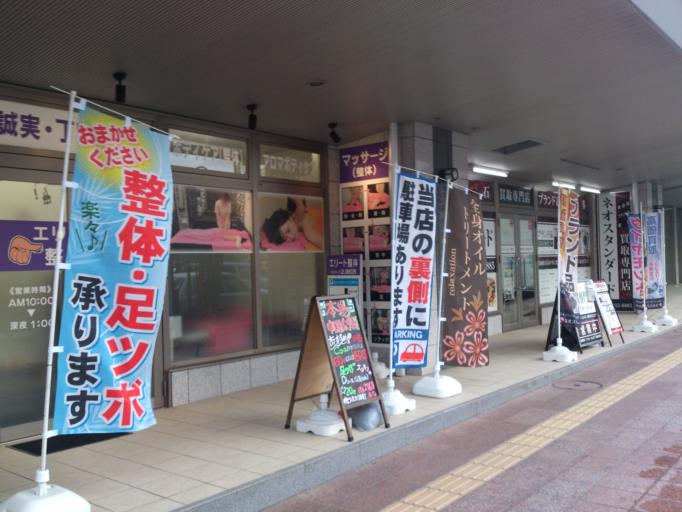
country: JP
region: Ishikawa
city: Kanazawa-shi
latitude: 36.5724
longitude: 136.6554
